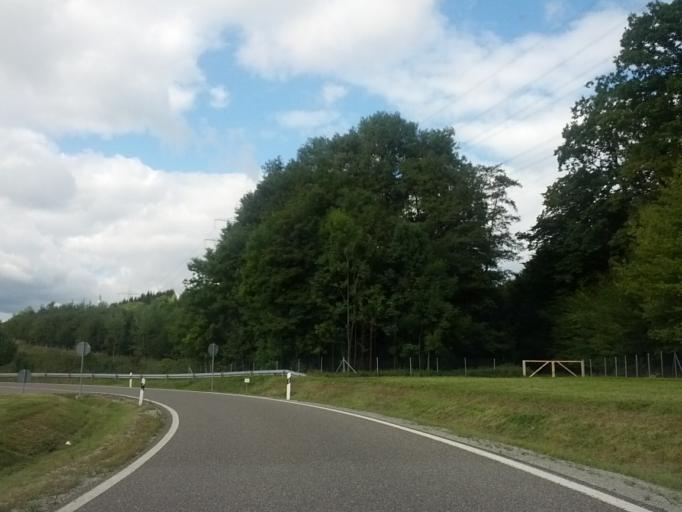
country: DE
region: Hesse
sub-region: Regierungsbezirk Kassel
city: Herleshausen
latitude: 51.0080
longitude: 10.1831
